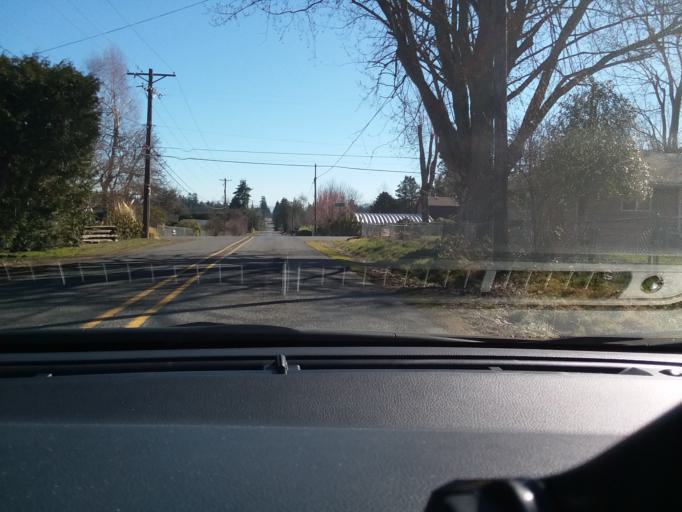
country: US
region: Washington
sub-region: Pierce County
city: Summit
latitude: 47.1699
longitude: -122.3763
